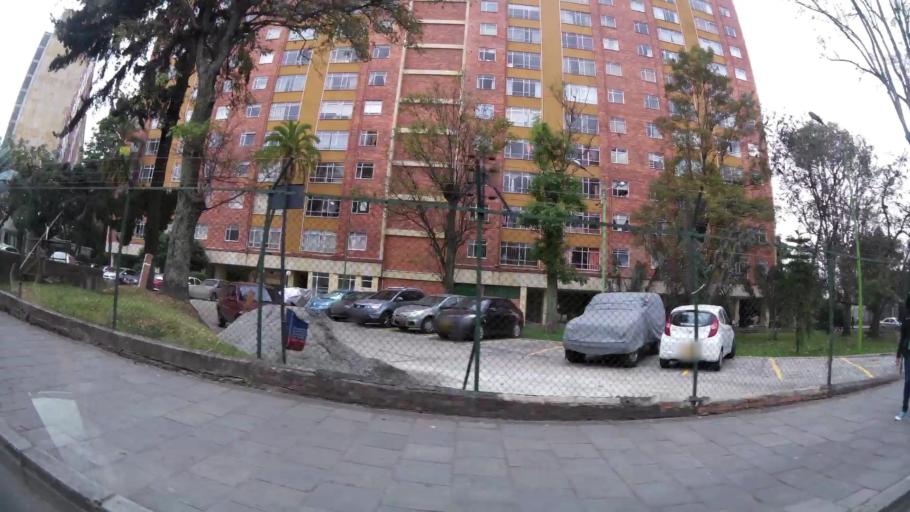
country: CO
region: Bogota D.C.
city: Bogota
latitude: 4.6296
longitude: -74.0881
